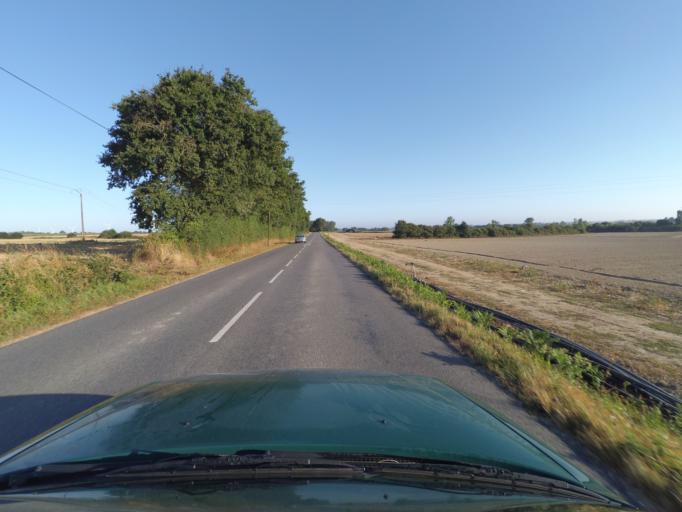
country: FR
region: Pays de la Loire
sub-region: Departement de la Loire-Atlantique
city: Vieillevigne
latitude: 46.9920
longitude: -1.4495
